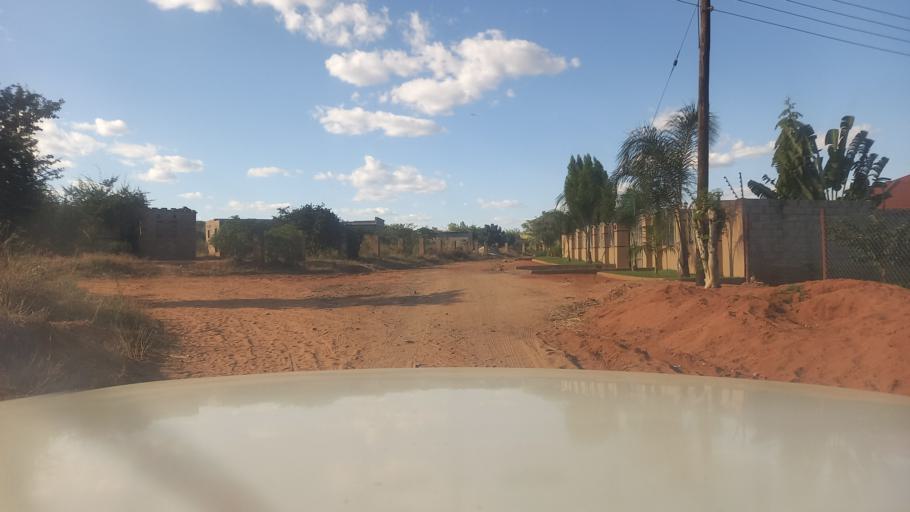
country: ZM
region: Southern
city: Livingstone
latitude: -17.8263
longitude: 25.8706
